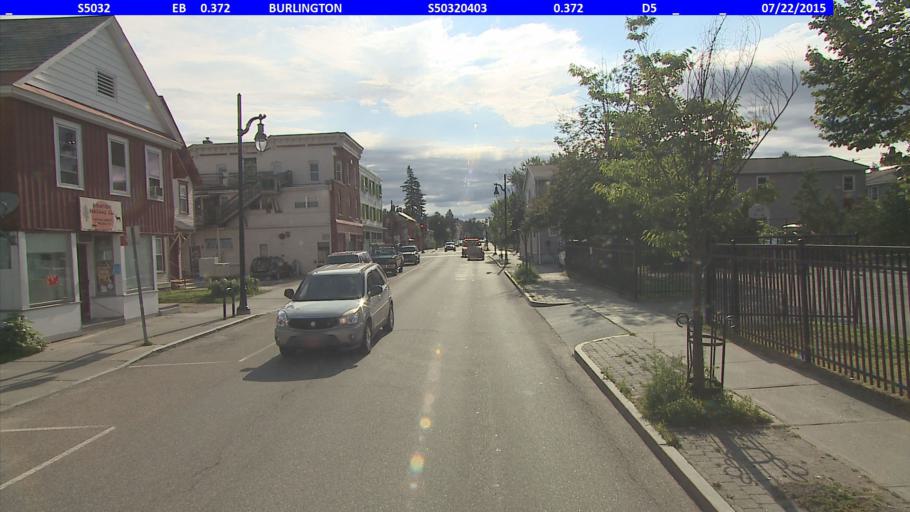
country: US
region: Vermont
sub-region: Chittenden County
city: Burlington
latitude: 44.4847
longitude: -73.2149
